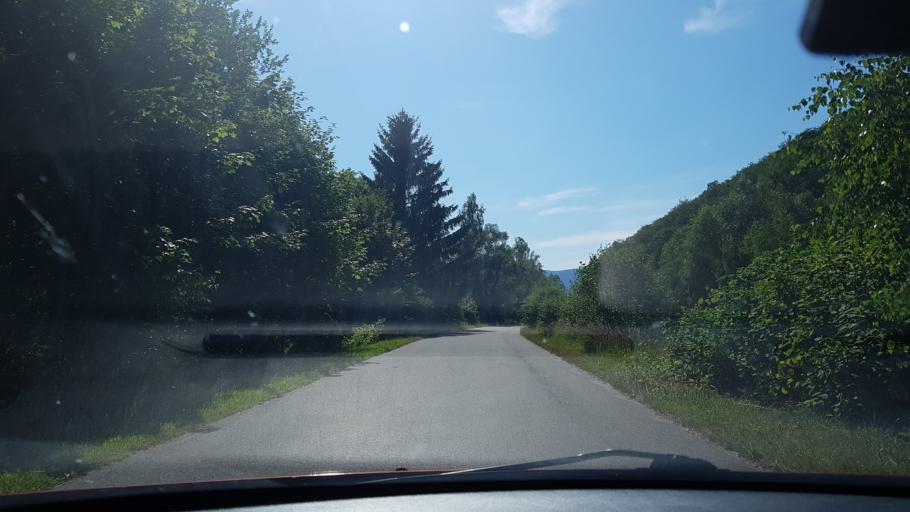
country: PL
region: Lower Silesian Voivodeship
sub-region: Powiat klodzki
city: Miedzylesie
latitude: 50.2330
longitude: 16.7353
